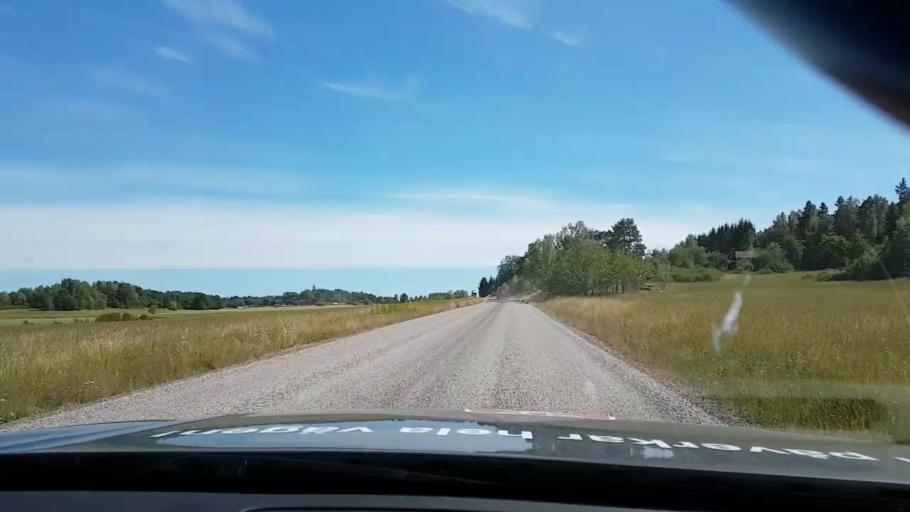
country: SE
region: Kalmar
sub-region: Vasterviks Kommun
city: Forserum
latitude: 57.9473
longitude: 16.4476
